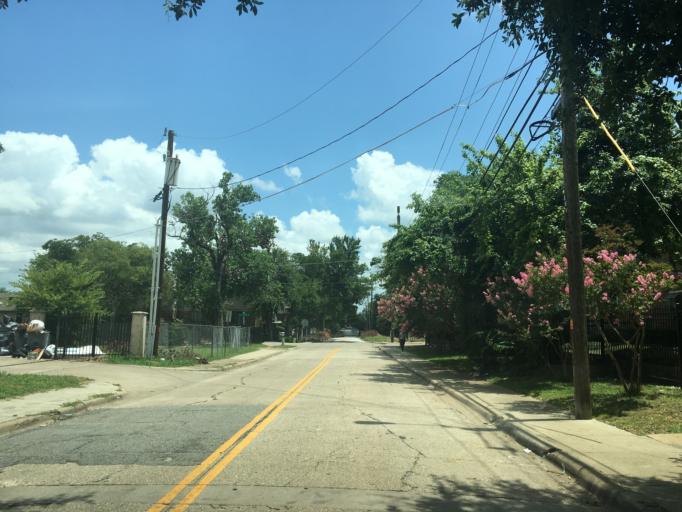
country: US
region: Texas
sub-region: Dallas County
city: University Park
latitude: 32.8762
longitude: -96.7594
